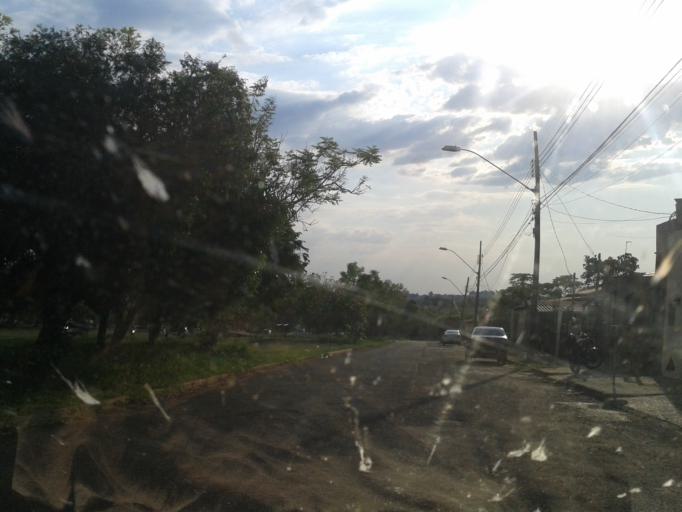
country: BR
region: Minas Gerais
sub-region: Uberlandia
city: Uberlandia
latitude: -18.9416
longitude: -48.3183
